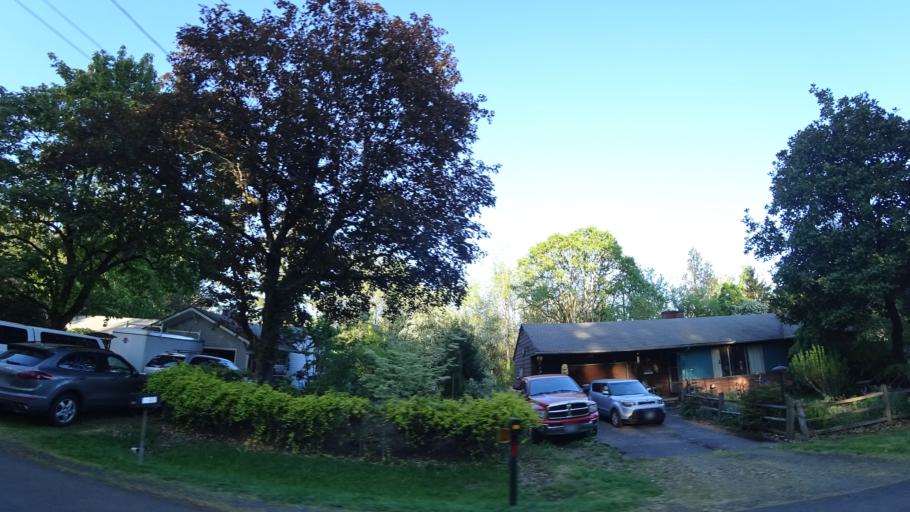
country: US
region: Oregon
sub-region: Washington County
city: West Slope
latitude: 45.4894
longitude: -122.7740
